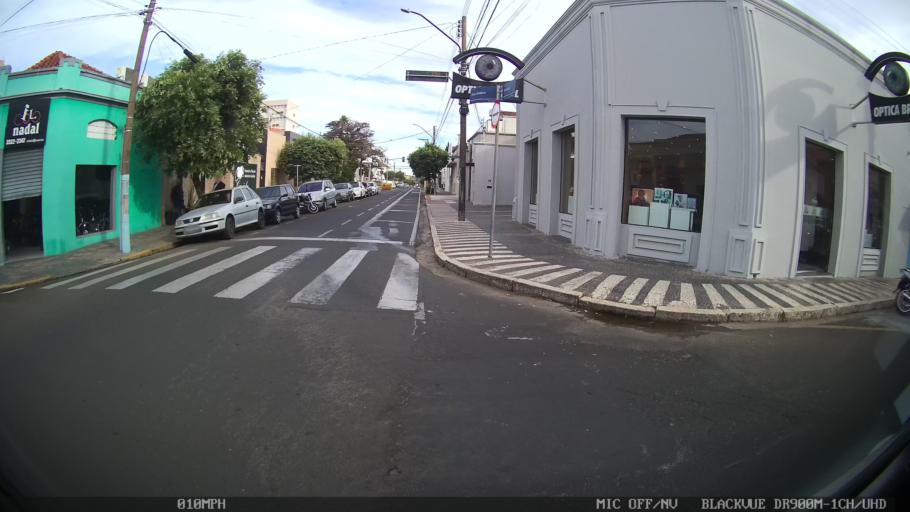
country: BR
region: Sao Paulo
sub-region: Catanduva
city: Catanduva
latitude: -21.1410
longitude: -48.9744
